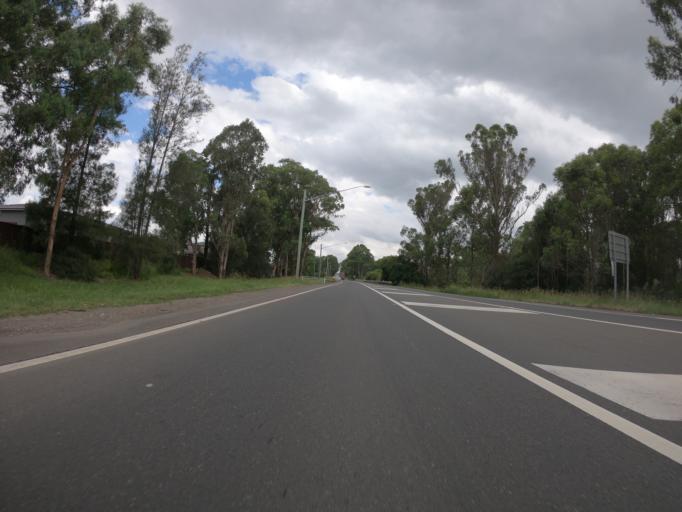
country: AU
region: New South Wales
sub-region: Blacktown
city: Mount Druitt
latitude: -33.8044
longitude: 150.7701
